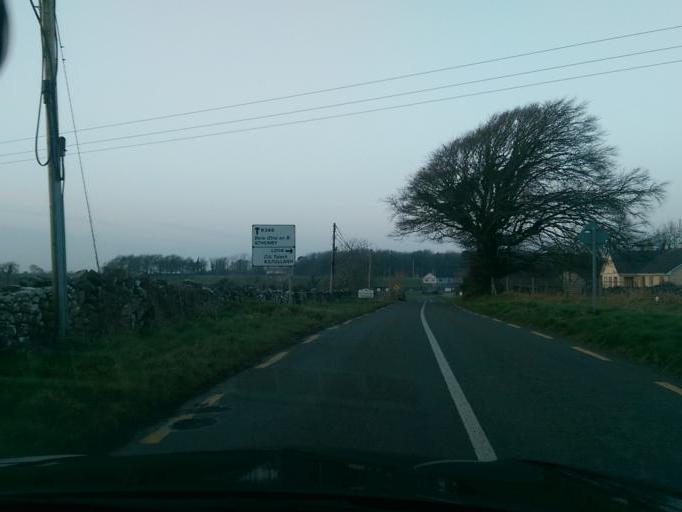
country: IE
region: Connaught
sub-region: County Galway
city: Loughrea
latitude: 53.2250
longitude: -8.6297
